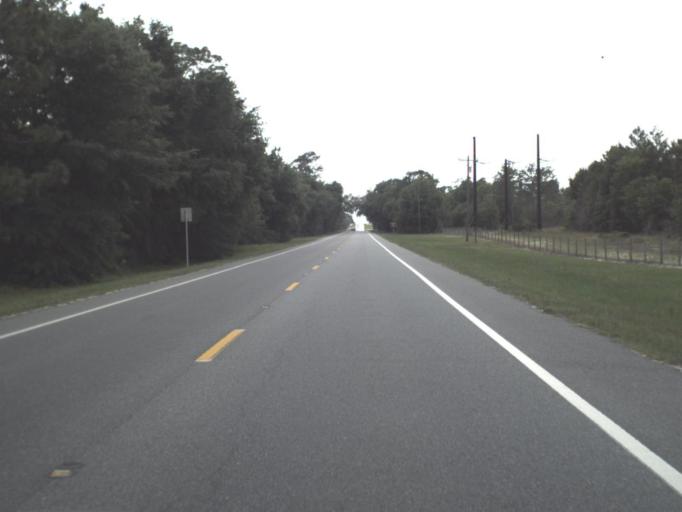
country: US
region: Florida
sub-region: Clay County
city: Keystone Heights
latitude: 29.8513
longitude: -81.9581
